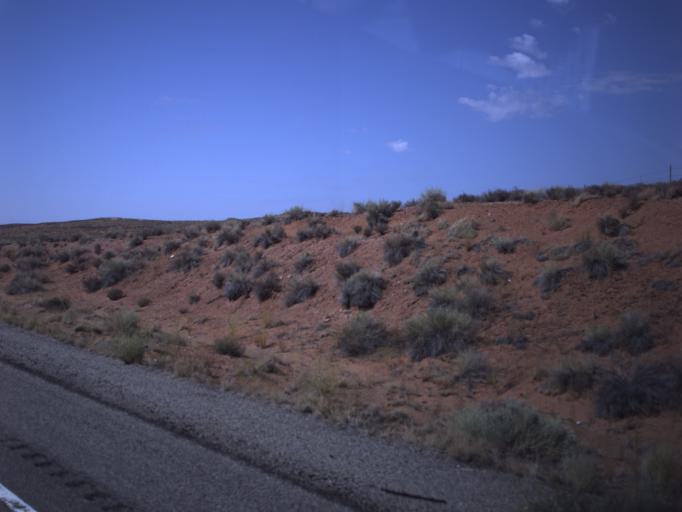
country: US
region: Utah
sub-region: San Juan County
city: Blanding
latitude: 37.2360
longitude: -109.6109
